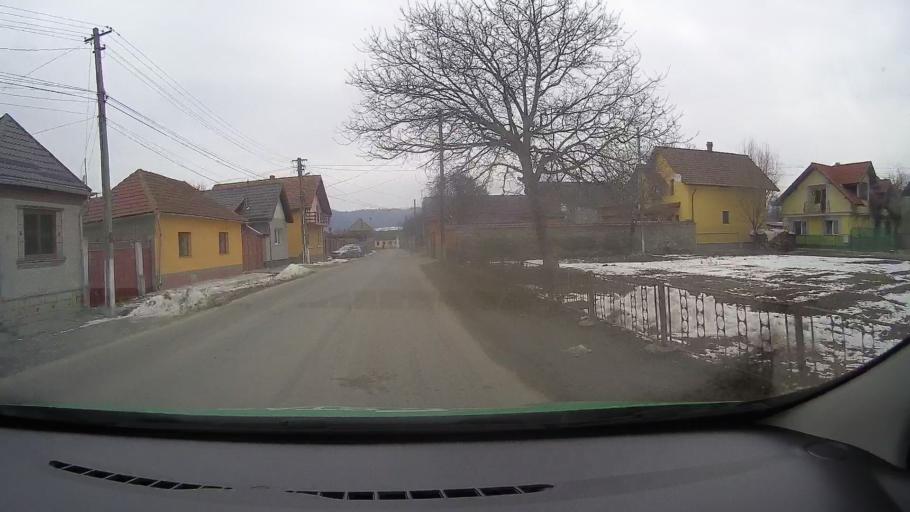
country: RO
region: Brasov
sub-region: Comuna Vulcan
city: Vulcan
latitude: 45.6345
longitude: 25.4255
